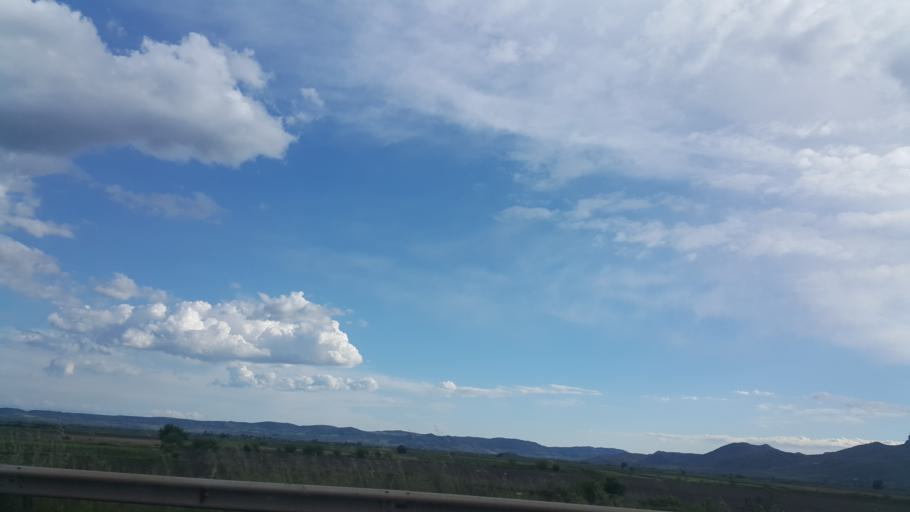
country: TR
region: Adana
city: Ceyhan
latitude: 36.9867
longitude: 35.7615
